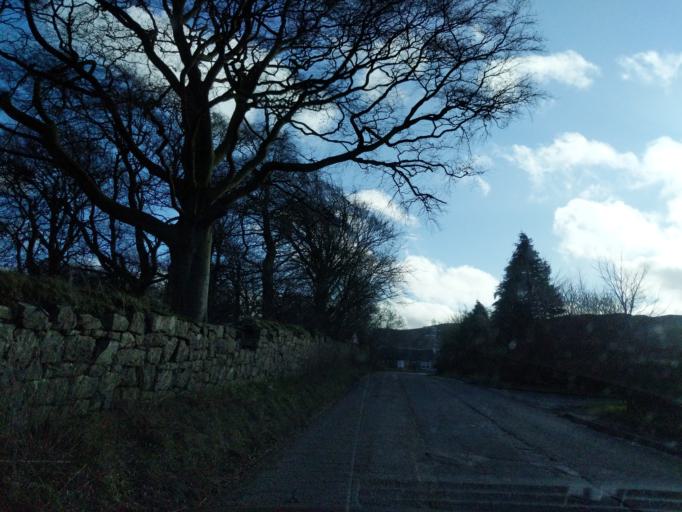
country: GB
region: Scotland
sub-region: Edinburgh
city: Ratho
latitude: 55.8947
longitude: -3.3824
